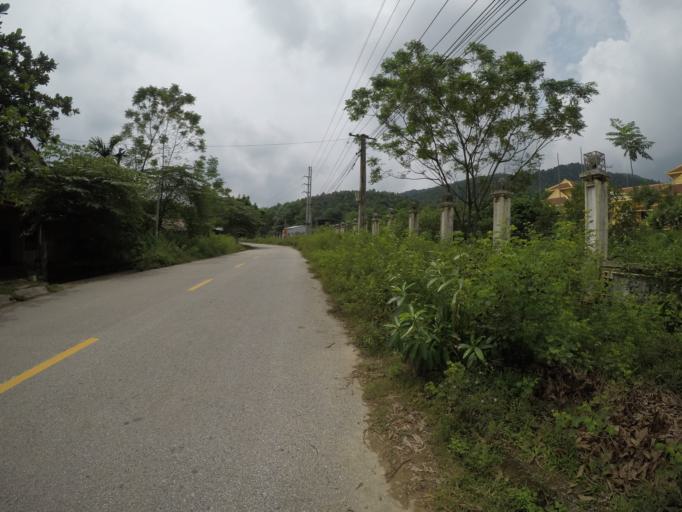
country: VN
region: Ha Noi
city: Soc Son
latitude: 21.2864
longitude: 105.8342
